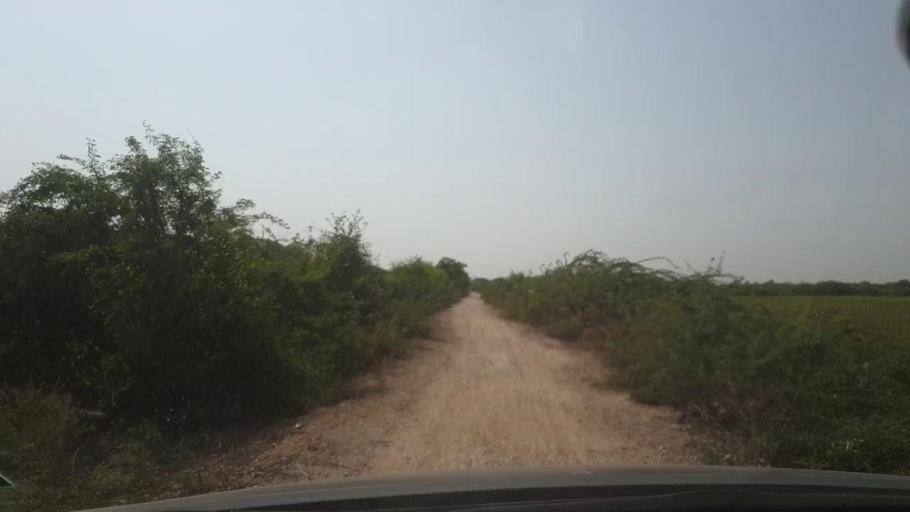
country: PK
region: Sindh
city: Naukot
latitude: 24.7959
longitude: 69.2438
